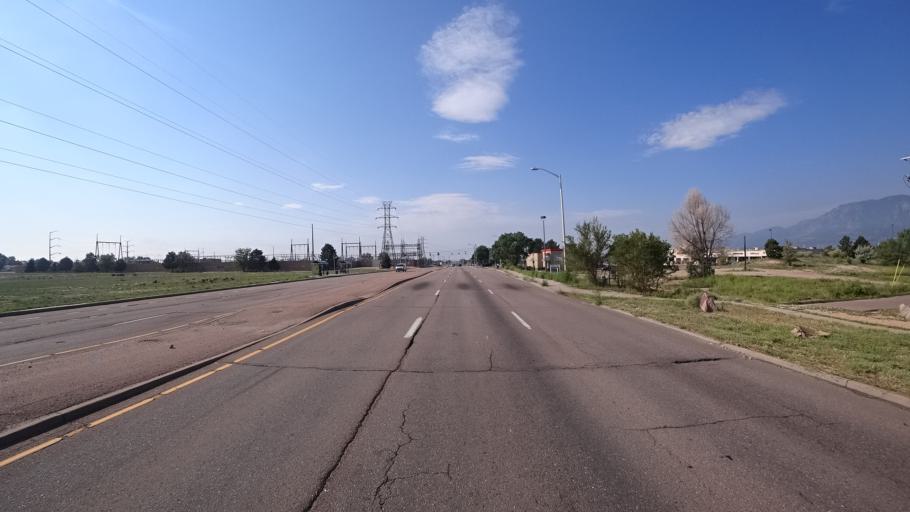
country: US
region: Colorado
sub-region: El Paso County
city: Stratmoor
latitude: 38.7943
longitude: -104.7576
